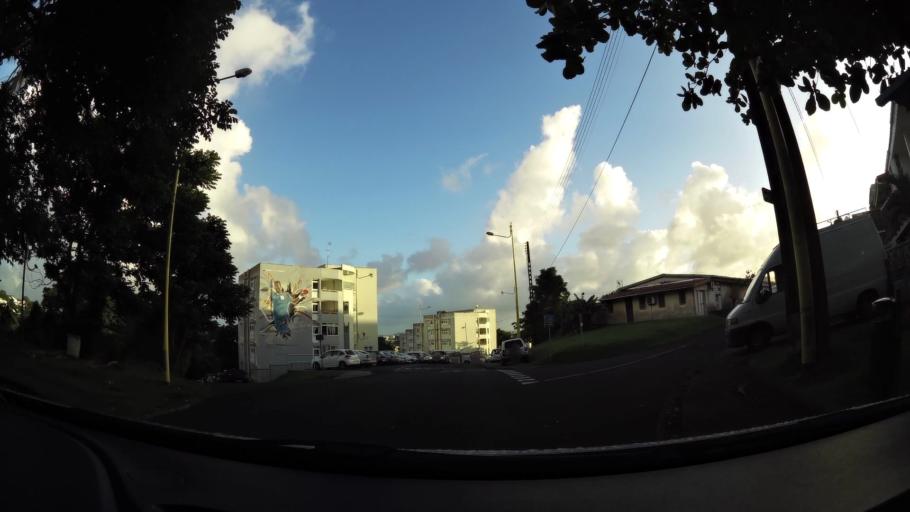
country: MQ
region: Martinique
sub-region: Martinique
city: Fort-de-France
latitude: 14.6326
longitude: -61.0679
